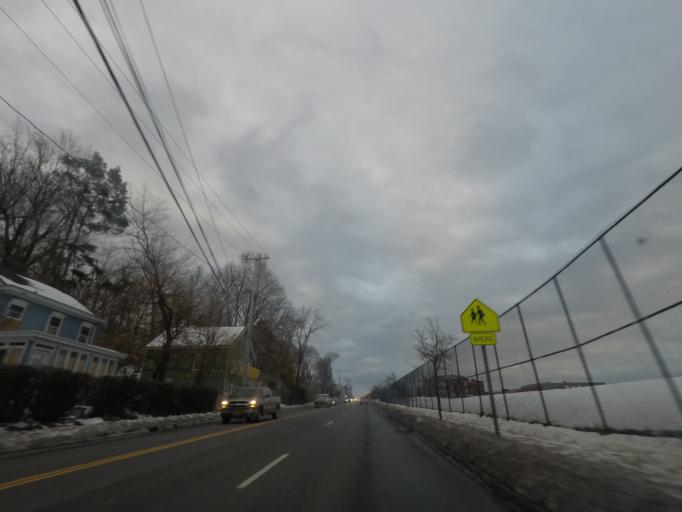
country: US
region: New York
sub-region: Orange County
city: Newburgh
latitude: 41.5157
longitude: -74.0201
